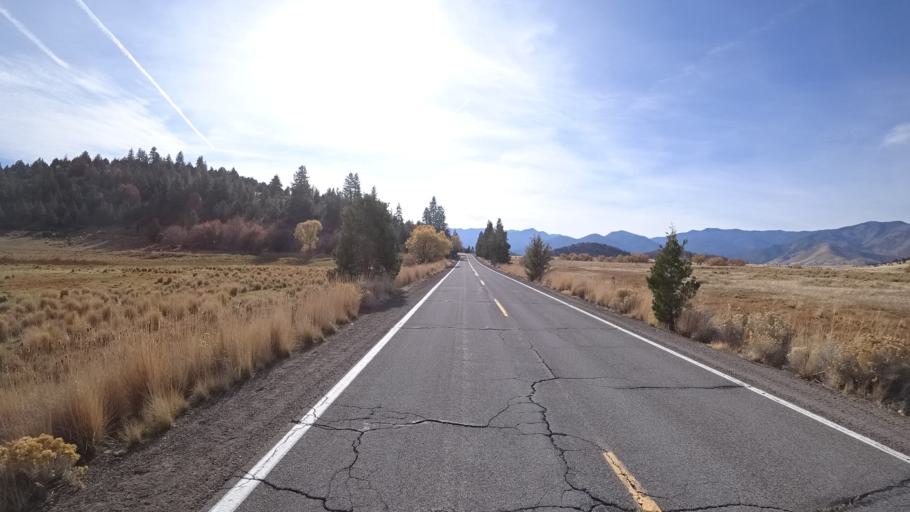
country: US
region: California
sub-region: Siskiyou County
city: Weed
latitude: 41.4819
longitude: -122.4102
